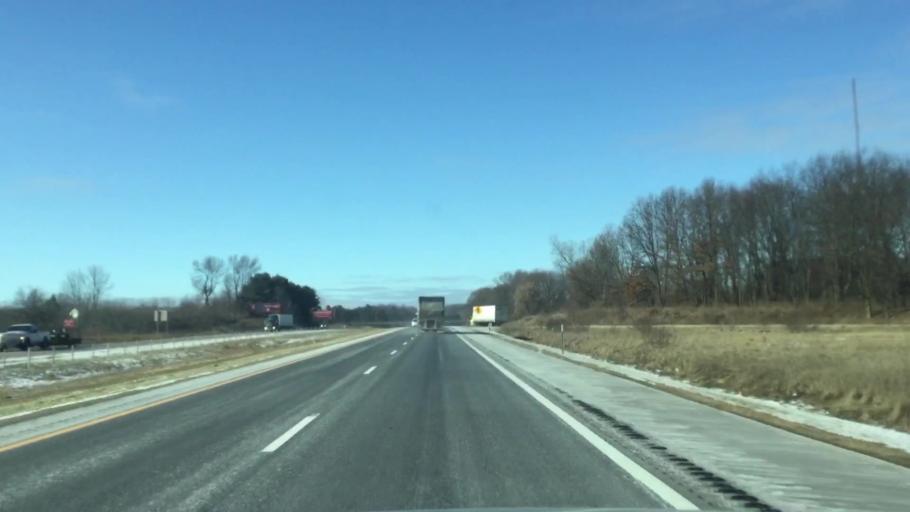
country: US
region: Michigan
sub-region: Calhoun County
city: Marshall
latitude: 42.2829
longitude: -84.9295
